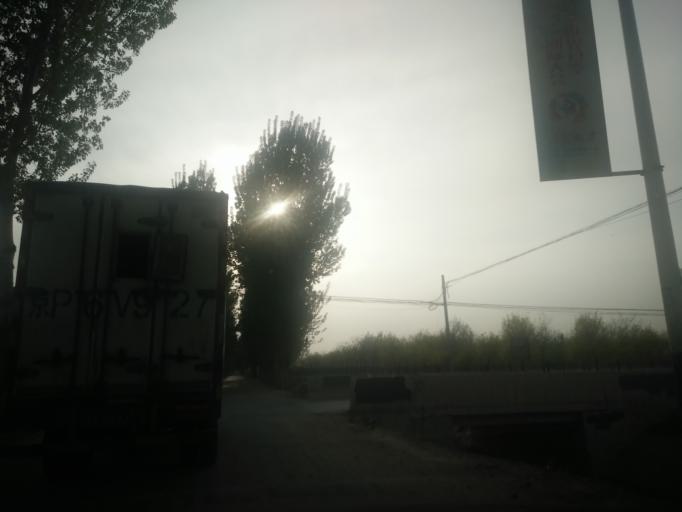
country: CN
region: Beijing
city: Weishanzhuang
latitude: 39.6750
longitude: 116.4339
